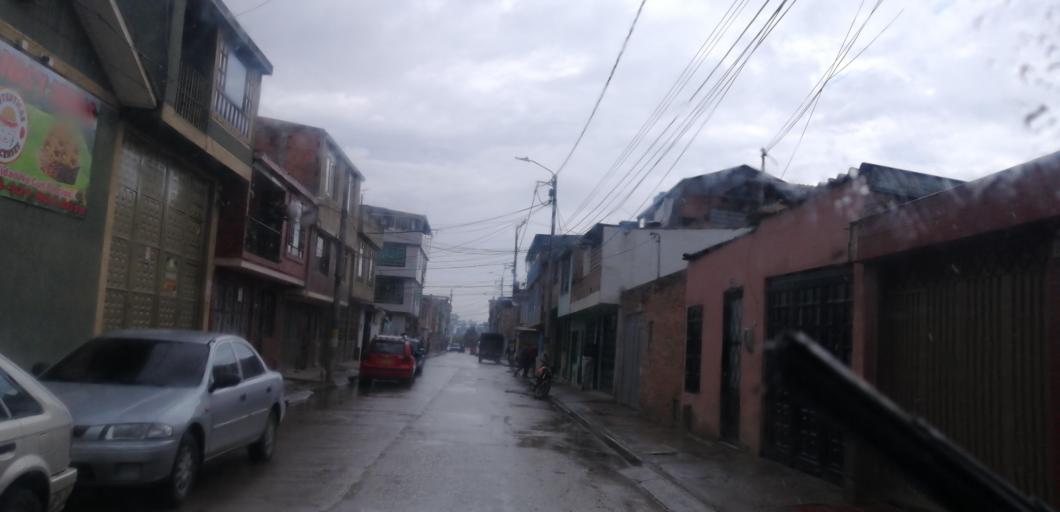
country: CO
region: Cundinamarca
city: Madrid
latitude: 4.7246
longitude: -74.2834
